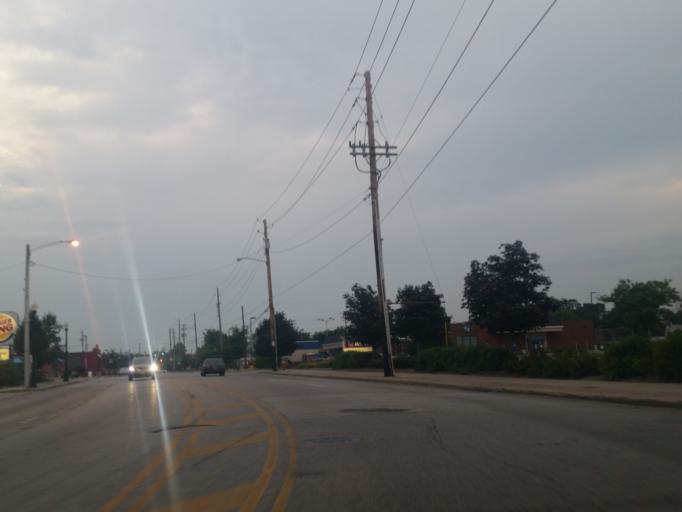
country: US
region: Ohio
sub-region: Cuyahoga County
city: Newburgh Heights
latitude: 41.4614
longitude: -81.6424
